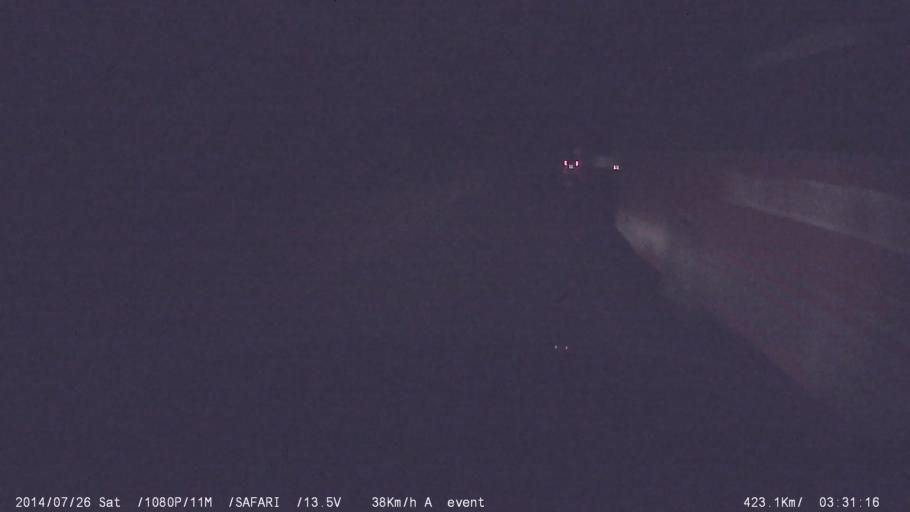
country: IN
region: Kerala
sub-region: Thrissur District
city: Chelakara
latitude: 10.6163
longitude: 76.5045
